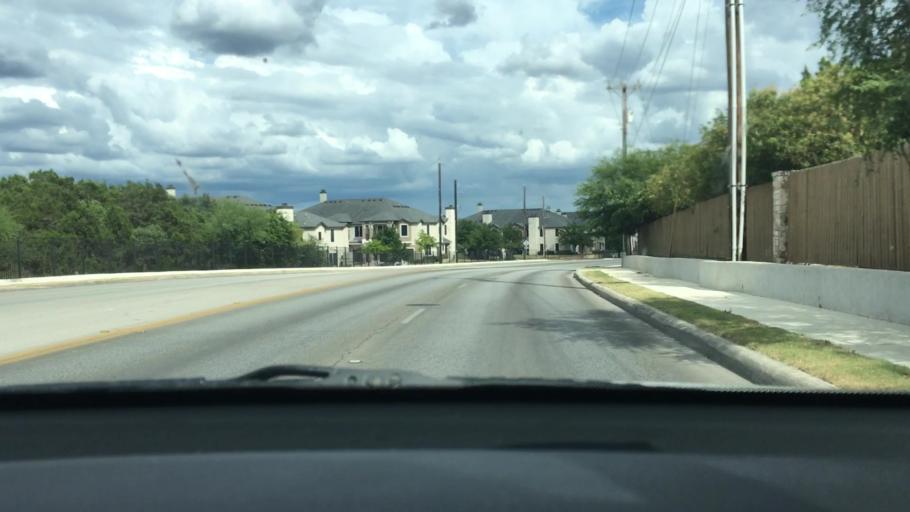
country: US
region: Texas
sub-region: Bexar County
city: Timberwood Park
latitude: 29.6538
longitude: -98.4280
